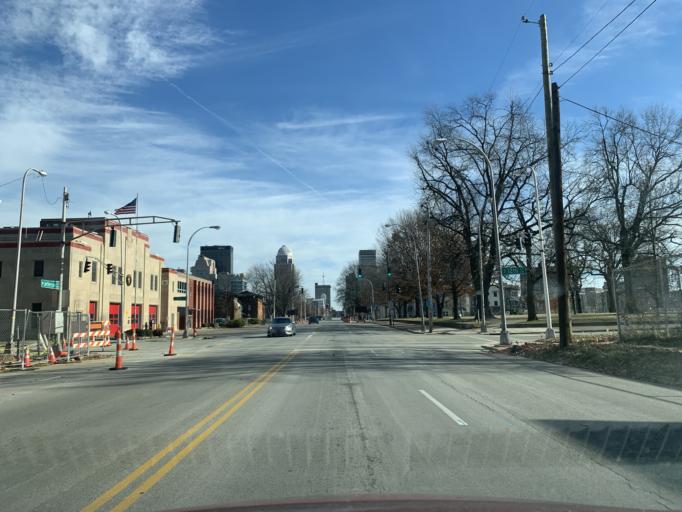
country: US
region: Kentucky
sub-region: Jefferson County
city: Louisville
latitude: 38.2553
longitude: -85.7707
